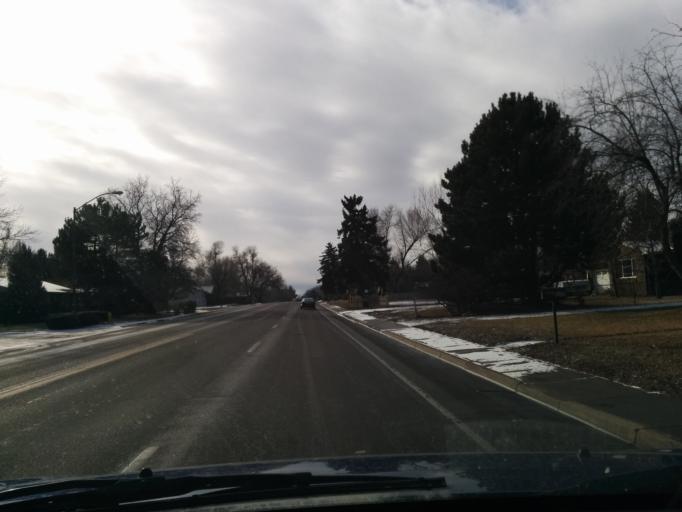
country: US
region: Colorado
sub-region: Larimer County
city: Fort Collins
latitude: 40.5703
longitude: -105.1152
